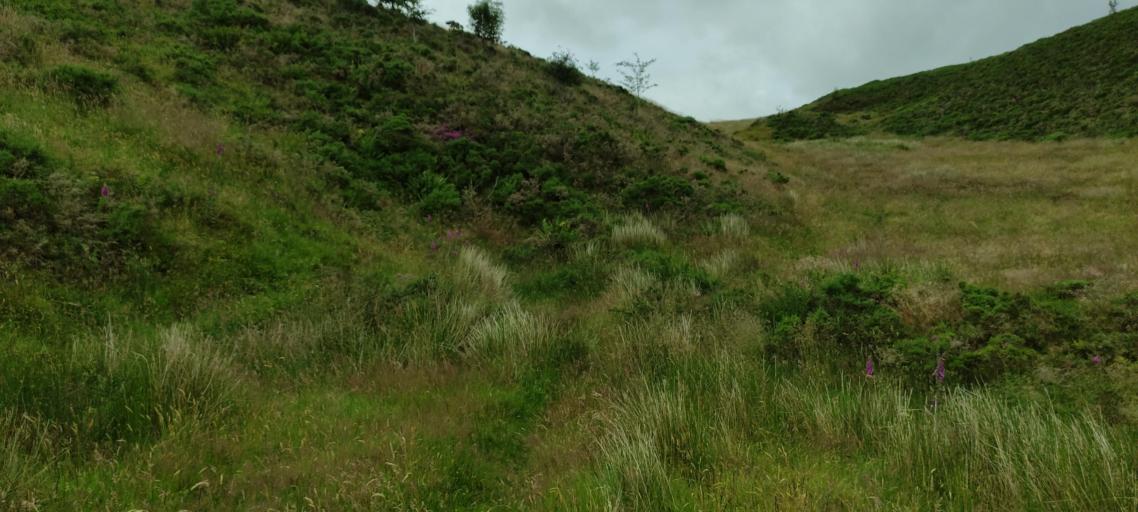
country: GB
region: England
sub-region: Cumbria
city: Frizington
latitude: 54.5496
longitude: -3.3972
